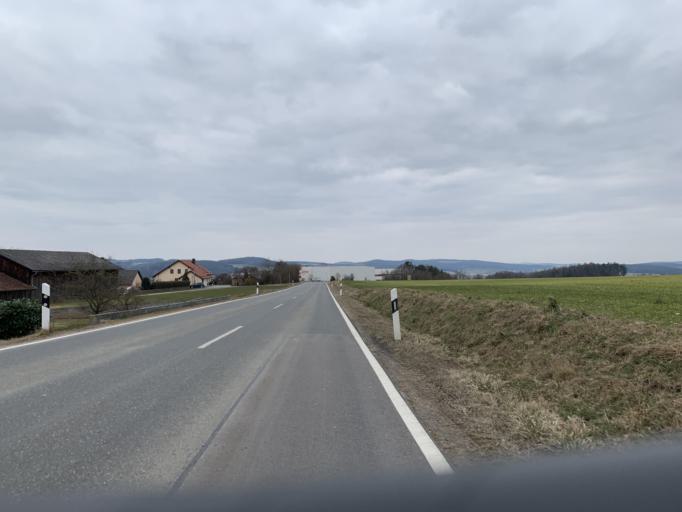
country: DE
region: Bavaria
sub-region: Upper Palatinate
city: Neunburg vorm Wald
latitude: 49.3365
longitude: 12.4123
